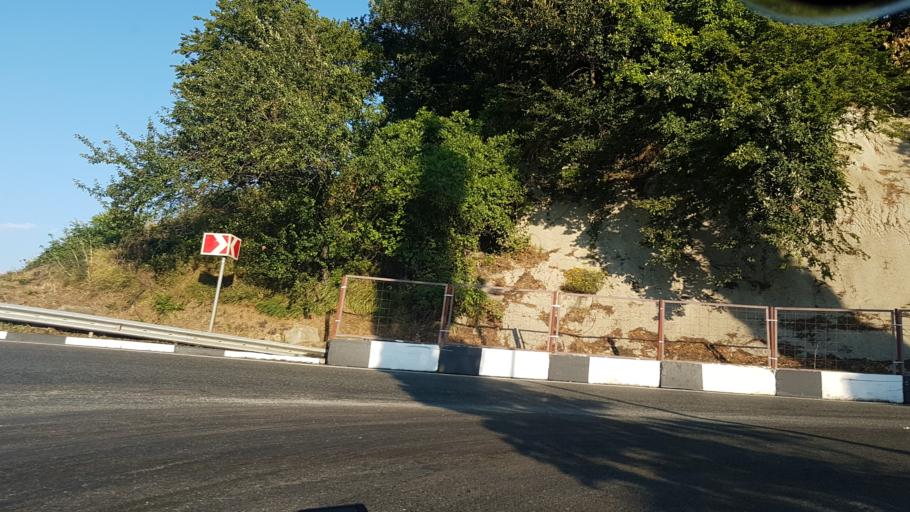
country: RU
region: Krasnodarskiy
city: Dagomys
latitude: 43.6552
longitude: 39.6453
